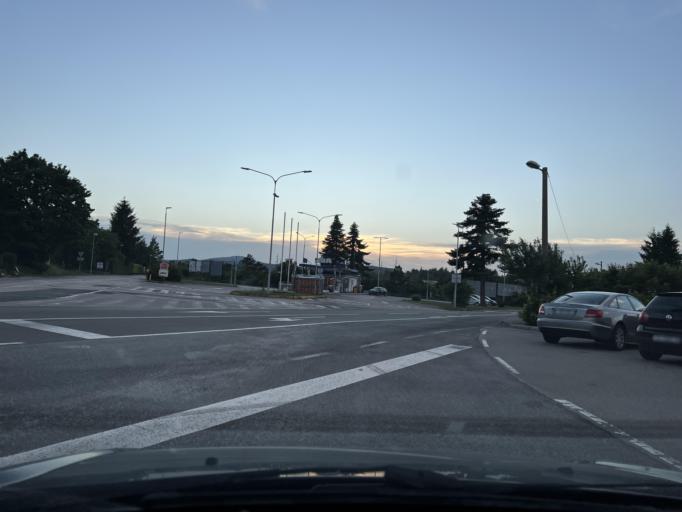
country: HR
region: Primorsko-Goranska
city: Klana
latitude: 45.4742
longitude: 14.2847
